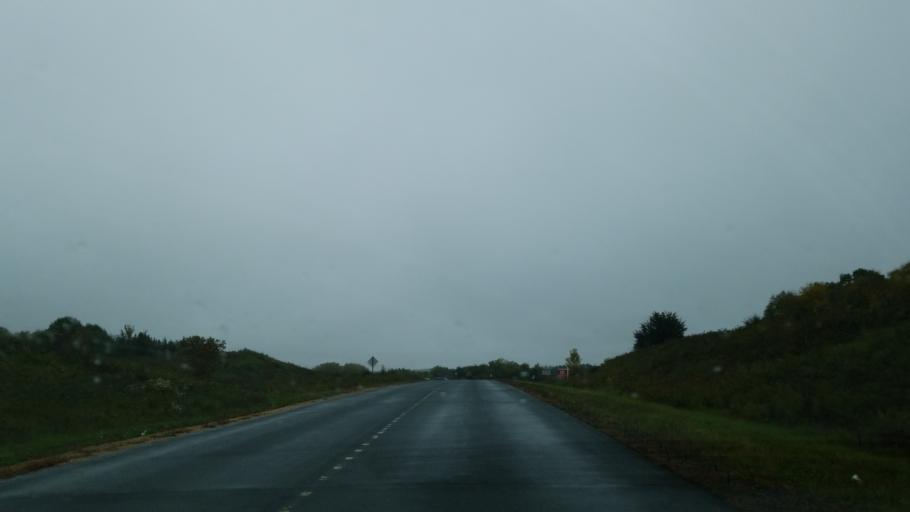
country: US
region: Minnesota
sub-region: Washington County
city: Stillwater
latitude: 45.0906
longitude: -92.7460
